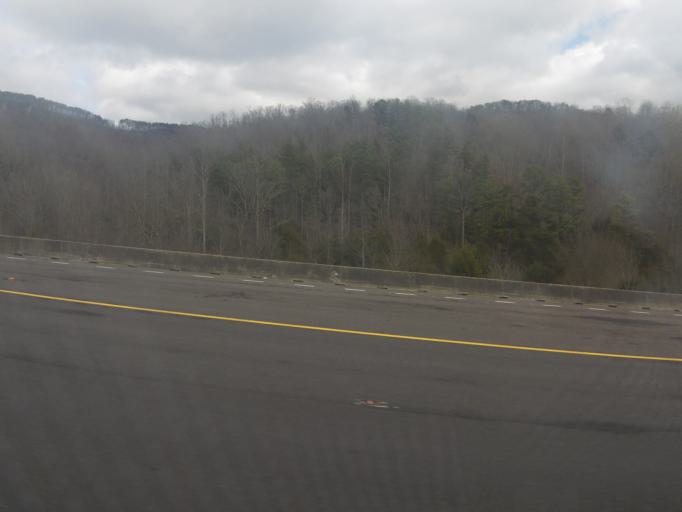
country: US
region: Tennessee
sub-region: Marion County
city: Monteagle
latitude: 35.1829
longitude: -85.8115
